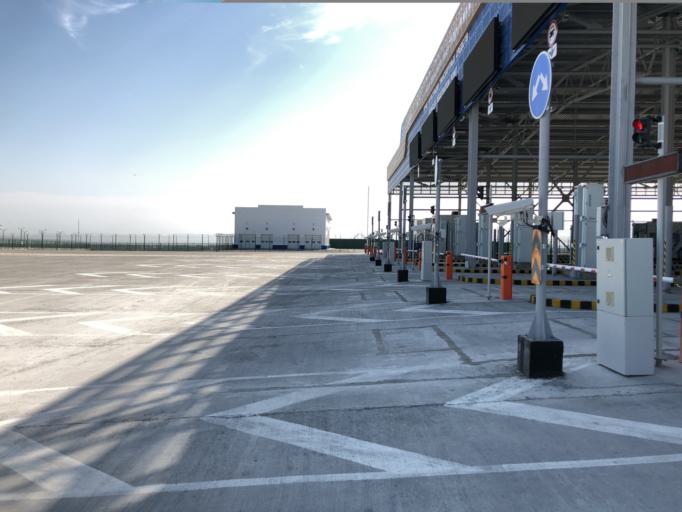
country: KZ
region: Almaty Oblysy
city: Zharkent
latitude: 44.1576
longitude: 80.3991
